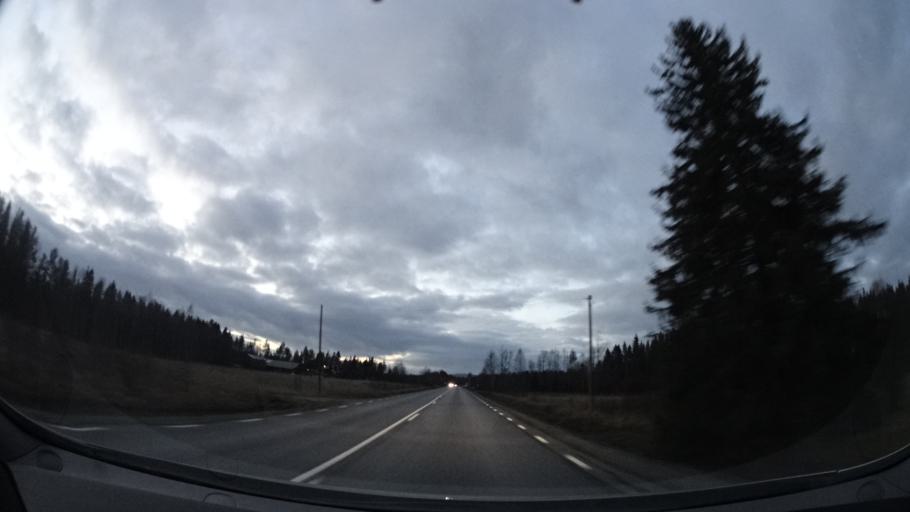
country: SE
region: Vaesterbotten
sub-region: Asele Kommun
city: Asele
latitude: 64.1697
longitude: 17.3129
